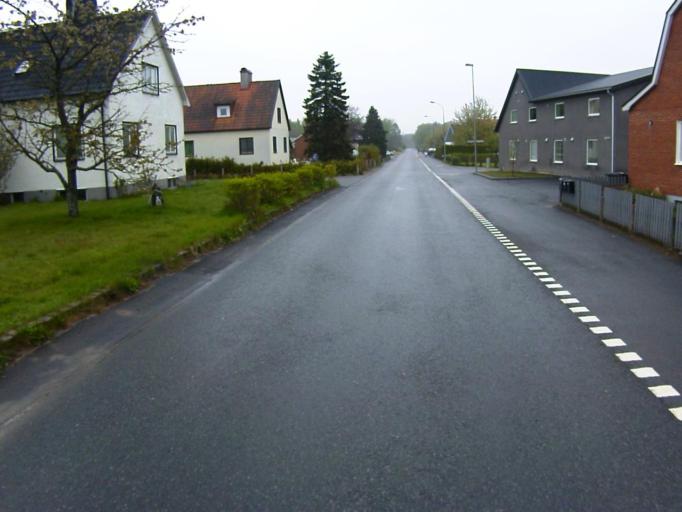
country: SE
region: Skane
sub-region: Kristianstads Kommun
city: Onnestad
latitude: 55.9322
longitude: 13.9657
